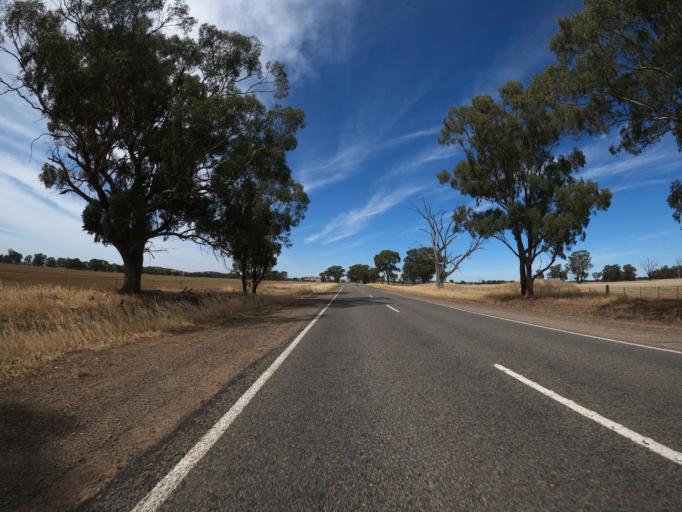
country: AU
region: Victoria
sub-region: Benalla
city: Benalla
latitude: -36.2961
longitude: 145.9523
